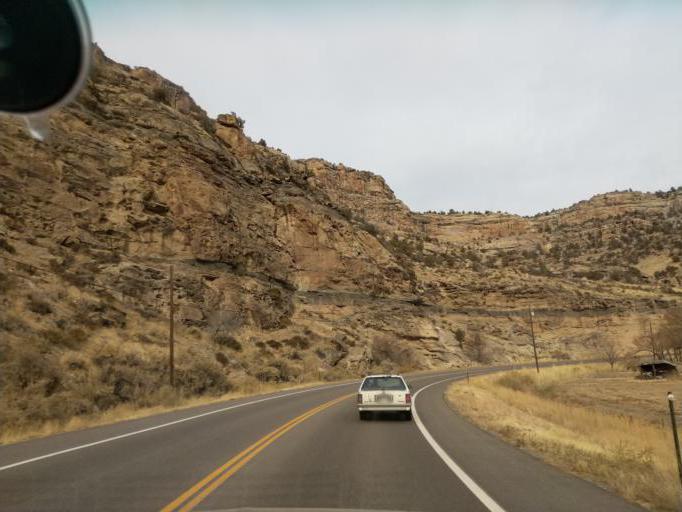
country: US
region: Colorado
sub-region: Mesa County
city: Palisade
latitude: 39.1904
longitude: -108.2591
